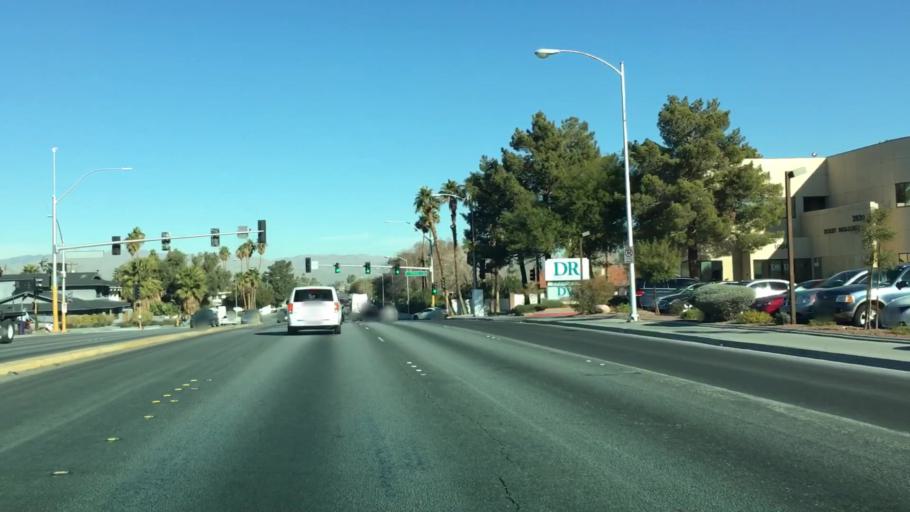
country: US
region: Nevada
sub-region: Clark County
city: Winchester
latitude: 36.1177
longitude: -115.1190
